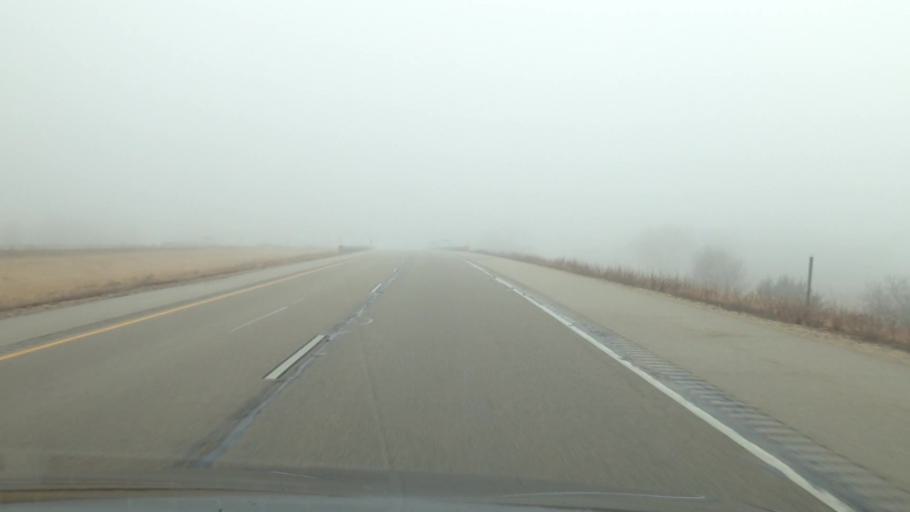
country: US
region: Wisconsin
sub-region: Walworth County
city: Elkhorn
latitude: 42.7043
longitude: -88.4859
